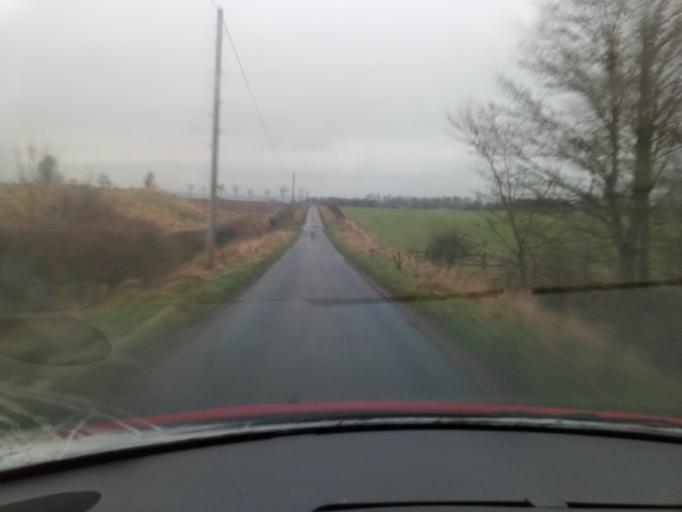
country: GB
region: Scotland
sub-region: The Scottish Borders
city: Kelso
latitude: 55.5617
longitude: -2.4294
